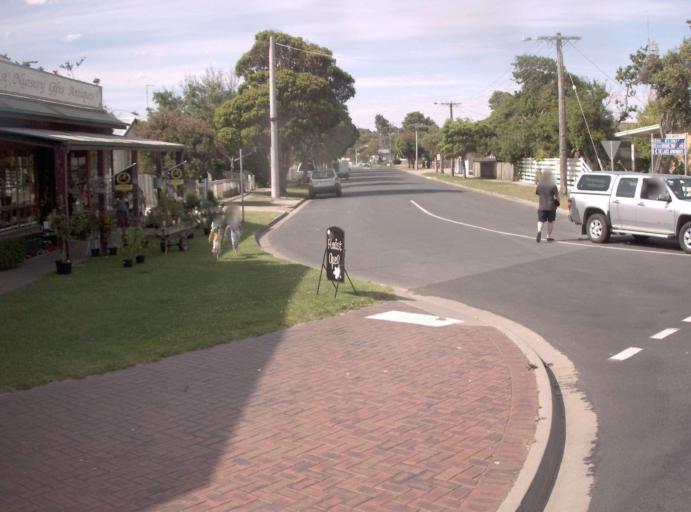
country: AU
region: Victoria
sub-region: East Gippsland
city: Lakes Entrance
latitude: -37.8805
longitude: 147.9882
